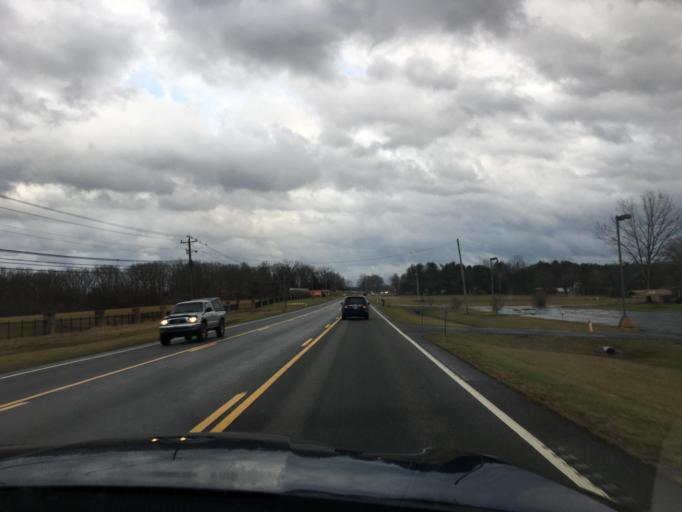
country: US
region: Tennessee
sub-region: Cumberland County
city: Crossville
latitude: 35.9255
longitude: -85.0045
